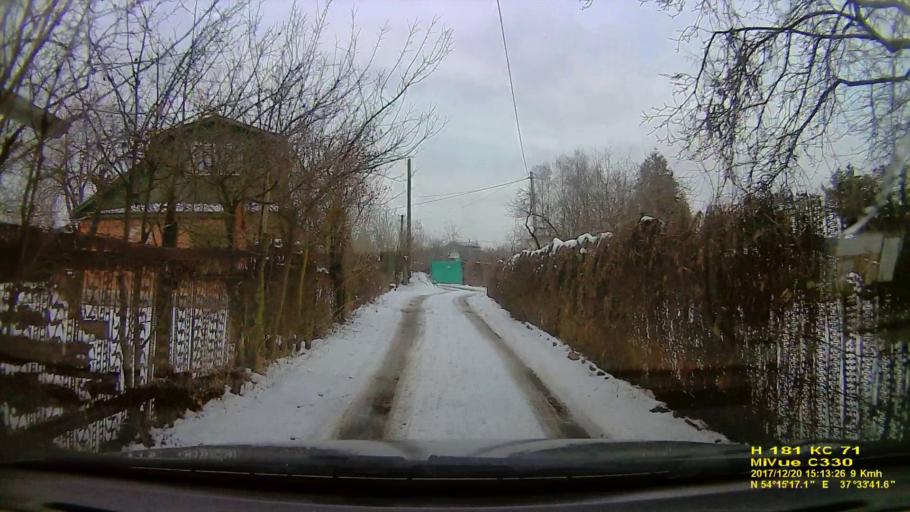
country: RU
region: Tula
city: Gorelki
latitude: 54.2547
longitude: 37.5615
